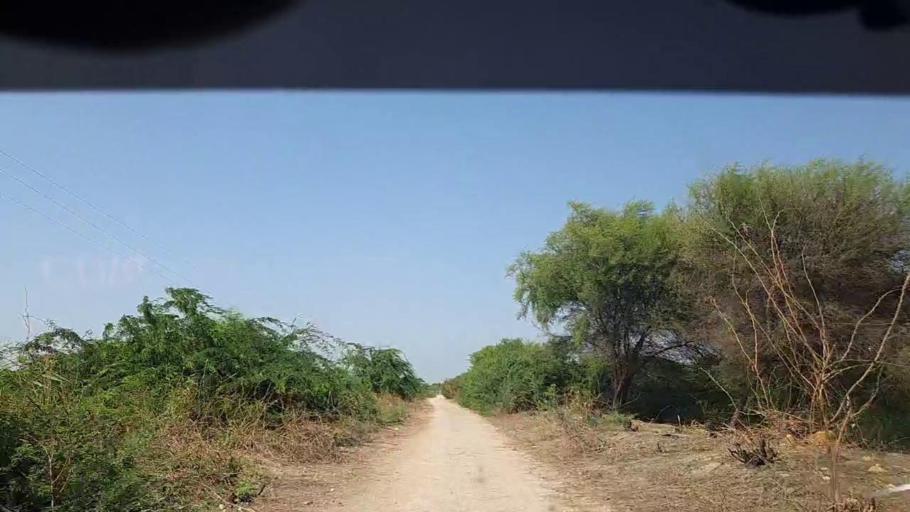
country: PK
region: Sindh
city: Badin
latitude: 24.4640
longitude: 68.7796
